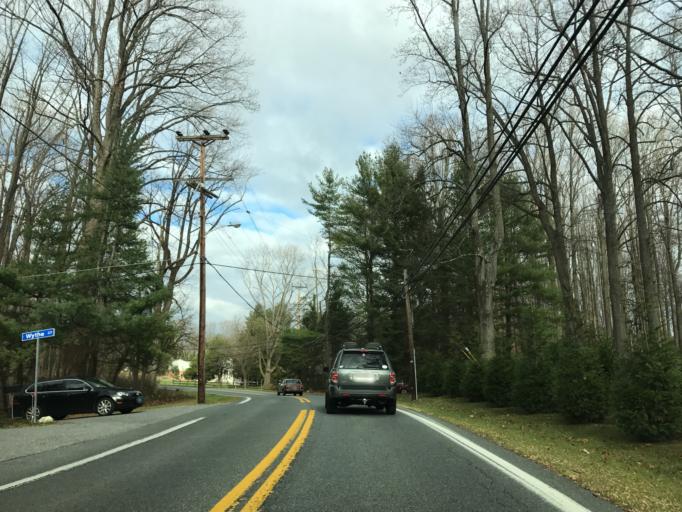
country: US
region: Maryland
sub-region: Baltimore County
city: Carney
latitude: 39.4442
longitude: -76.5318
